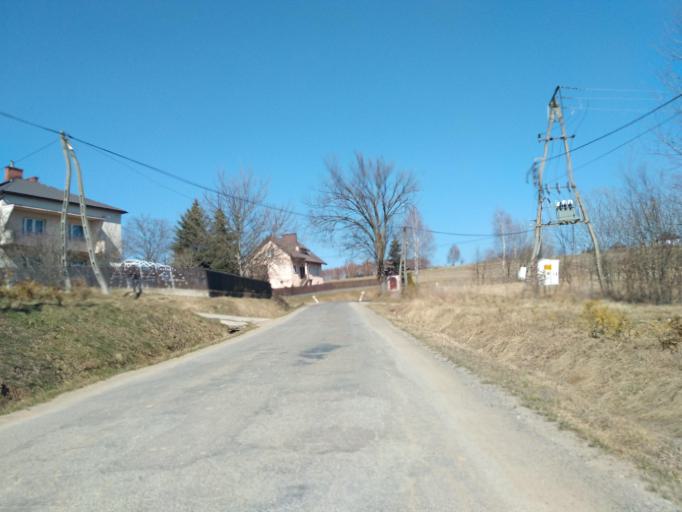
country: PL
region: Subcarpathian Voivodeship
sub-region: Powiat debicki
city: Brzostek
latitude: 49.9619
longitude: 21.4262
